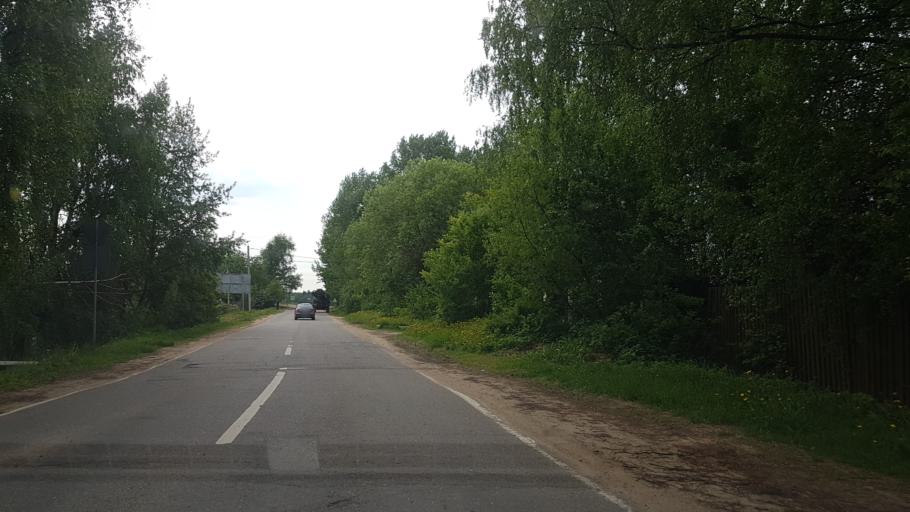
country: RU
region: Moskovskaya
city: Klin
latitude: 56.1537
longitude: 36.7518
